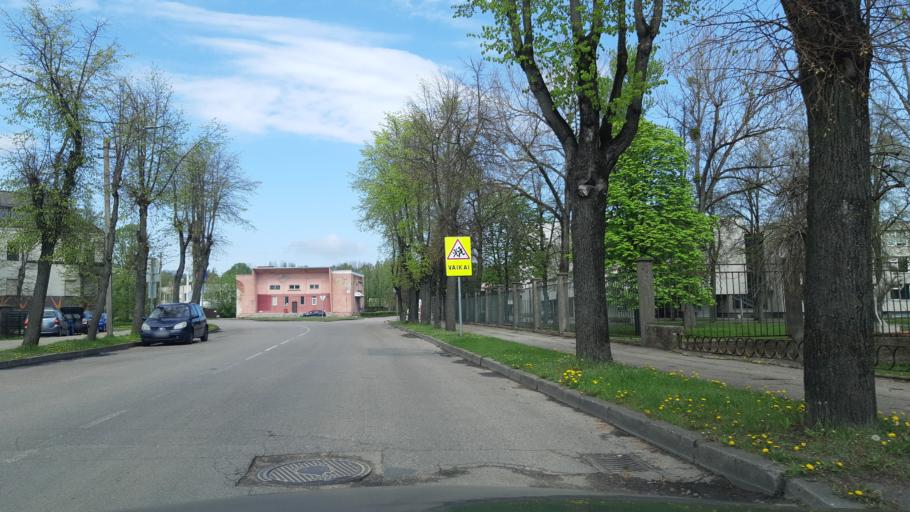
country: LT
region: Kauno apskritis
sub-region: Kaunas
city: Silainiai
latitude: 54.9083
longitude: 23.8791
